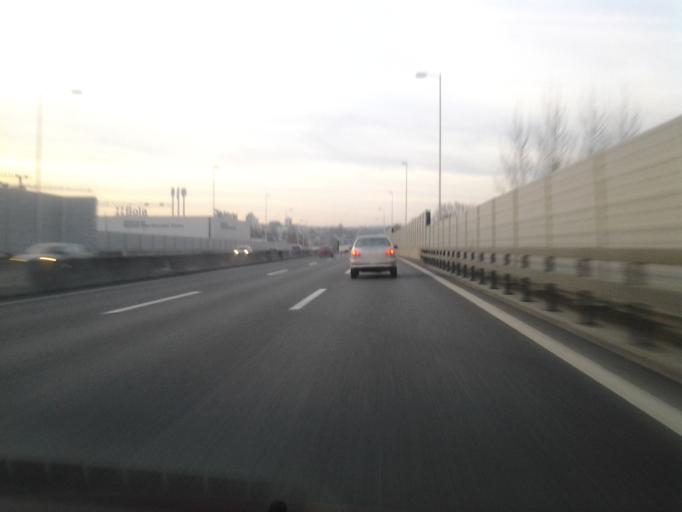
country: CH
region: Lucerne
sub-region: Hochdorf District
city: Emmen
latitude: 47.0743
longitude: 8.2944
